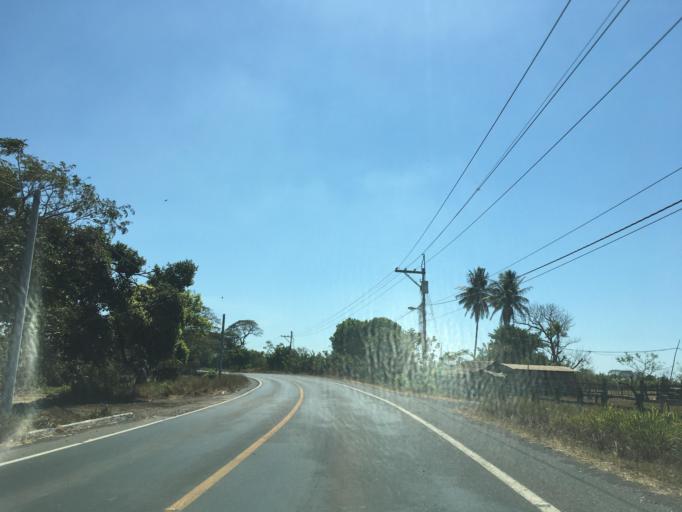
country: GT
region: Escuintla
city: Puerto San Jose
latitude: 13.9799
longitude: -90.8872
